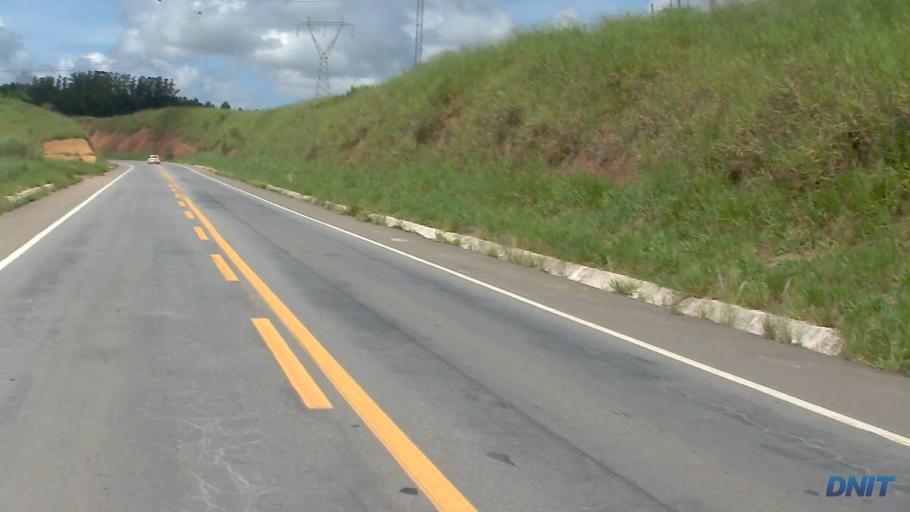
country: BR
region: Minas Gerais
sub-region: Belo Oriente
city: Belo Oriente
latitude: -19.0926
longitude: -42.1908
